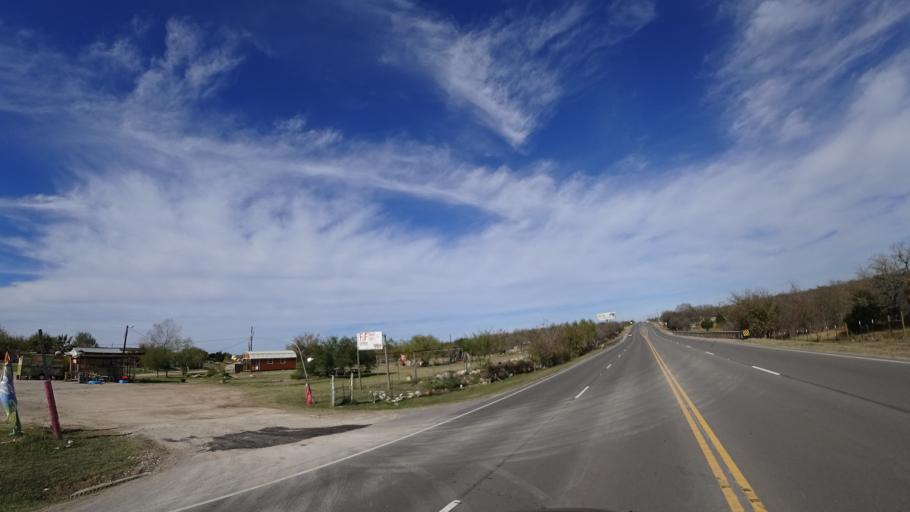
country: US
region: Texas
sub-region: Travis County
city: Onion Creek
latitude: 30.1042
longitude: -97.6945
